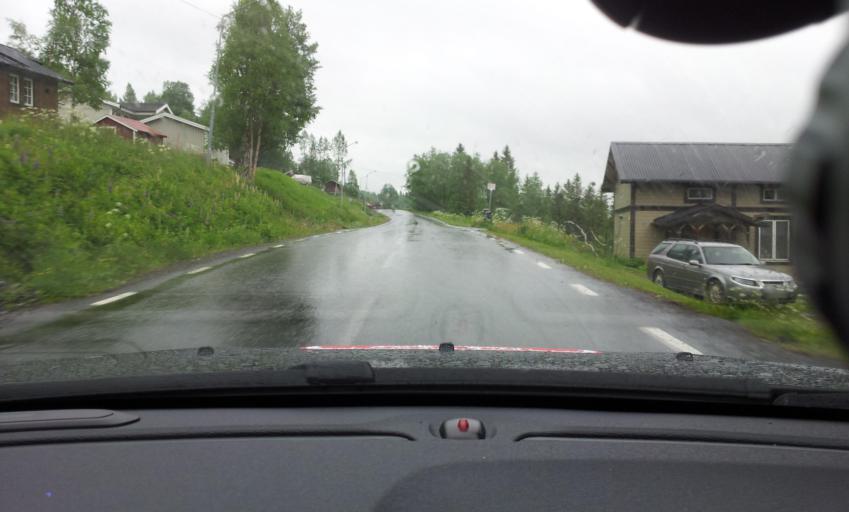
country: SE
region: Jaemtland
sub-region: Are Kommun
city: Are
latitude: 63.3150
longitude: 13.0780
